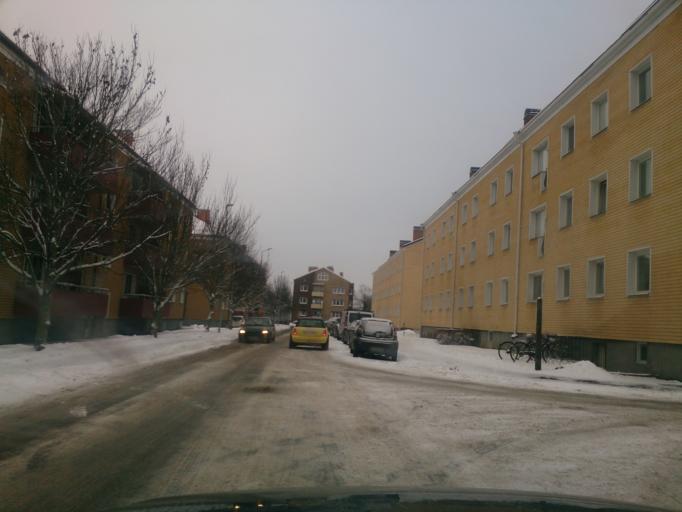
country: SE
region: OEstergoetland
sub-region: Norrkopings Kommun
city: Norrkoping
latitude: 58.5981
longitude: 16.1559
